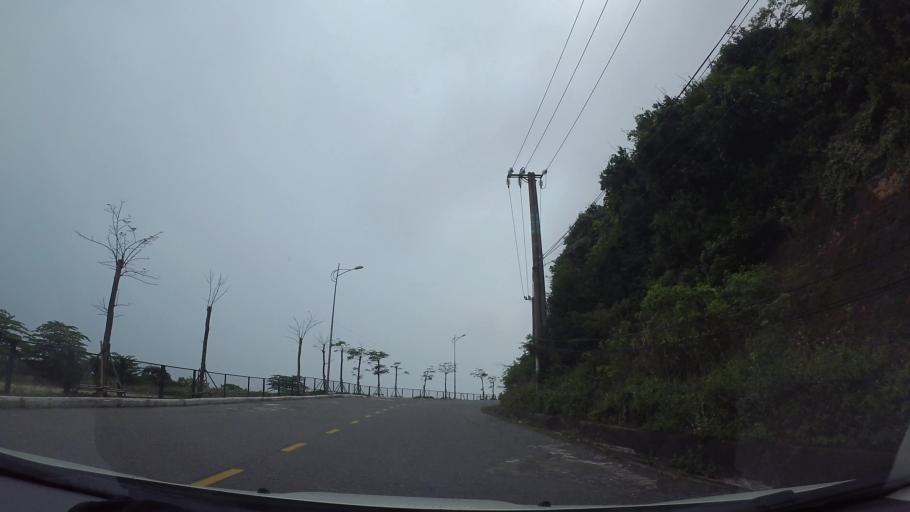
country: VN
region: Da Nang
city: Son Tra
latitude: 16.1155
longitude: 108.3109
